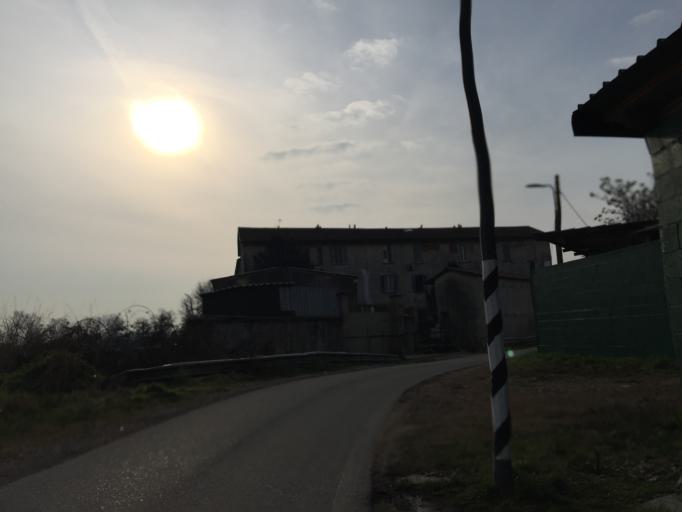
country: IT
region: Lombardy
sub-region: Citta metropolitana di Milano
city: Romano Banco
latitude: 45.4286
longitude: 9.1388
